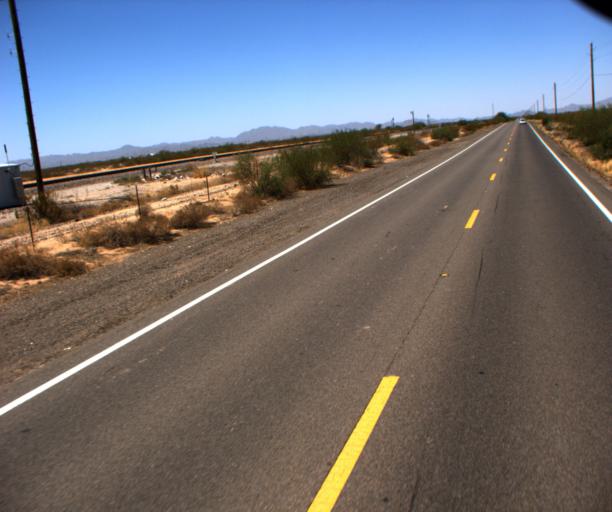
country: US
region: Arizona
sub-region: Pinal County
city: Maricopa
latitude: 33.0679
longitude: -112.2224
